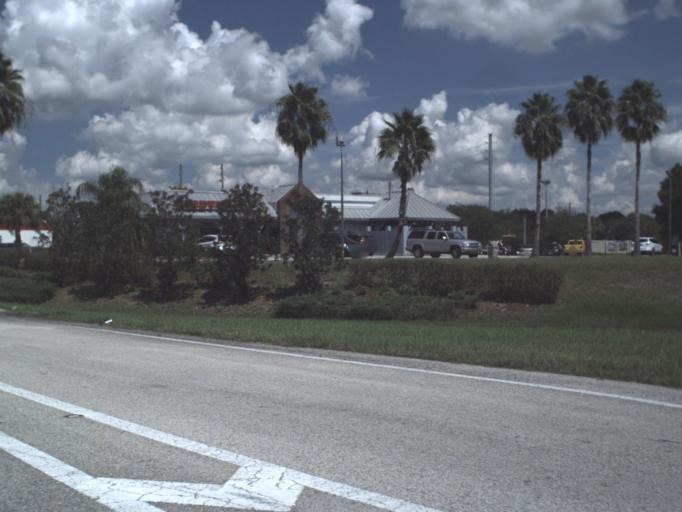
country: US
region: Florida
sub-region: Polk County
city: Lake Wales
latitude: 27.8991
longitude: -81.5998
